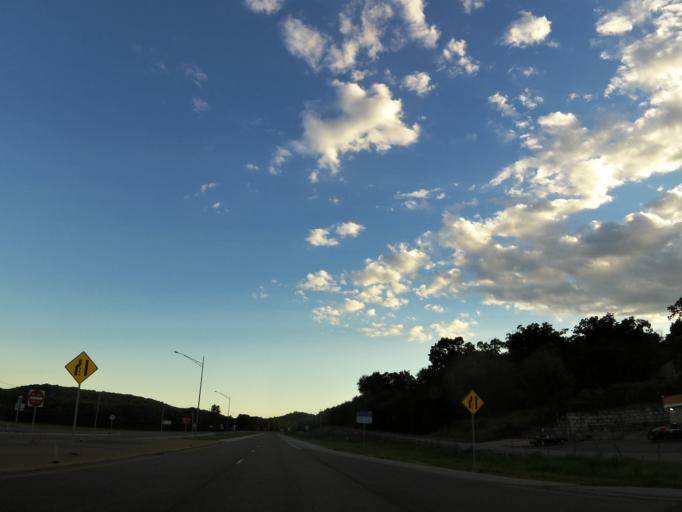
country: US
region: Missouri
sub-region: Jefferson County
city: Cedar Hill
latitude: 38.3413
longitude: -90.6541
